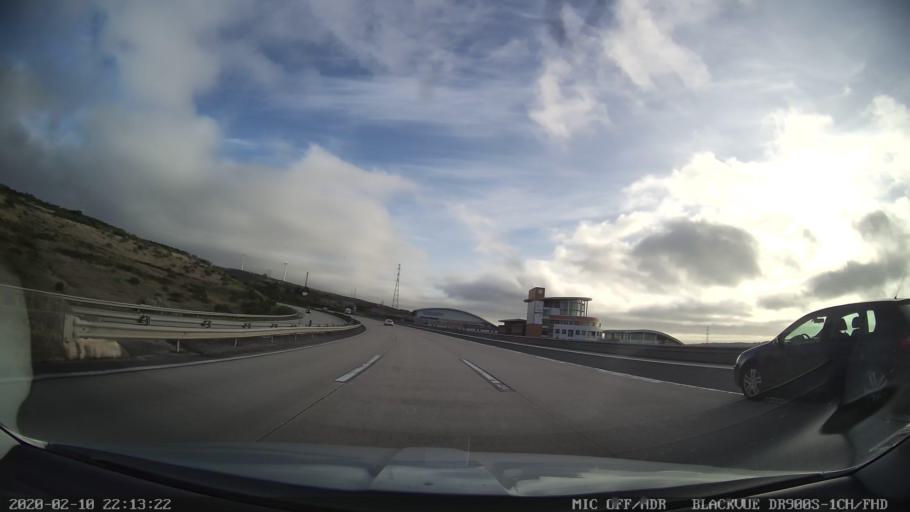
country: PT
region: Lisbon
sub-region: Loures
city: Santo Antao do Tojal
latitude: 38.8683
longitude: -9.1387
